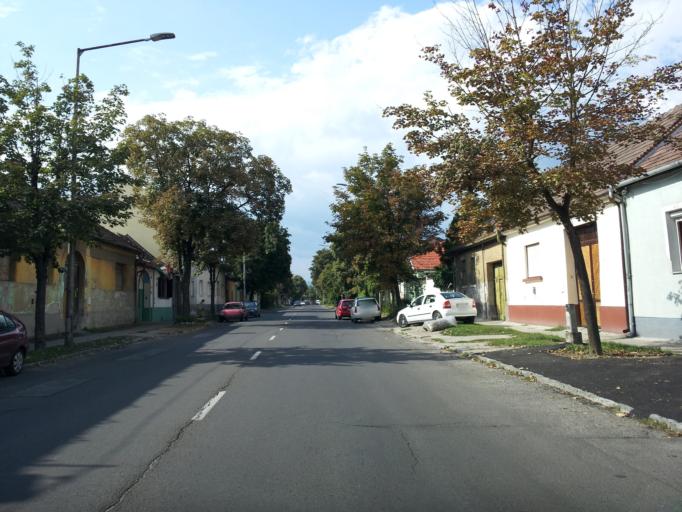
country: HU
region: Pest
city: Vac
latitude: 47.7854
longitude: 19.1223
